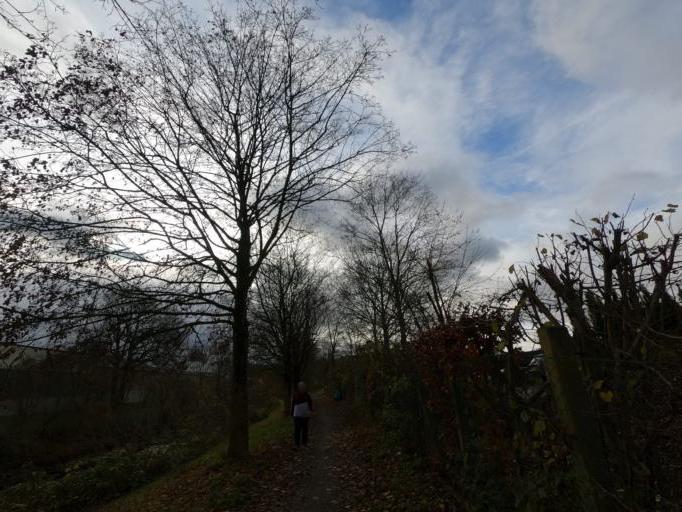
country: DE
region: Baden-Wuerttemberg
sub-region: Regierungsbezirk Stuttgart
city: Wangen
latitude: 48.7074
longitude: 9.6110
